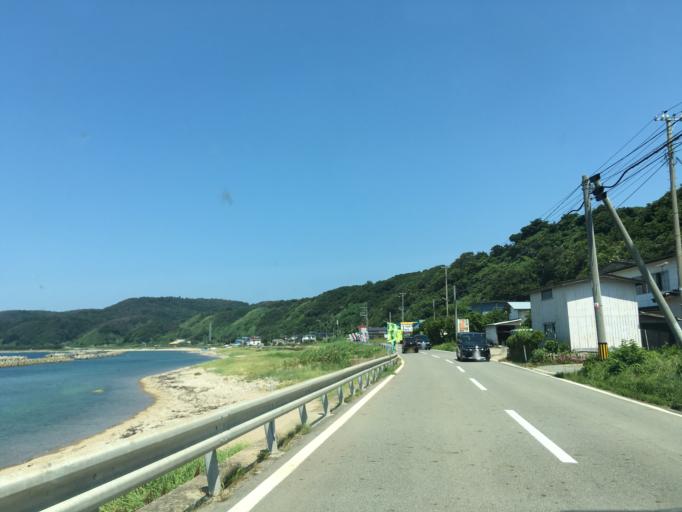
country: JP
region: Akita
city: Tenno
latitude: 39.9484
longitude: 139.7211
